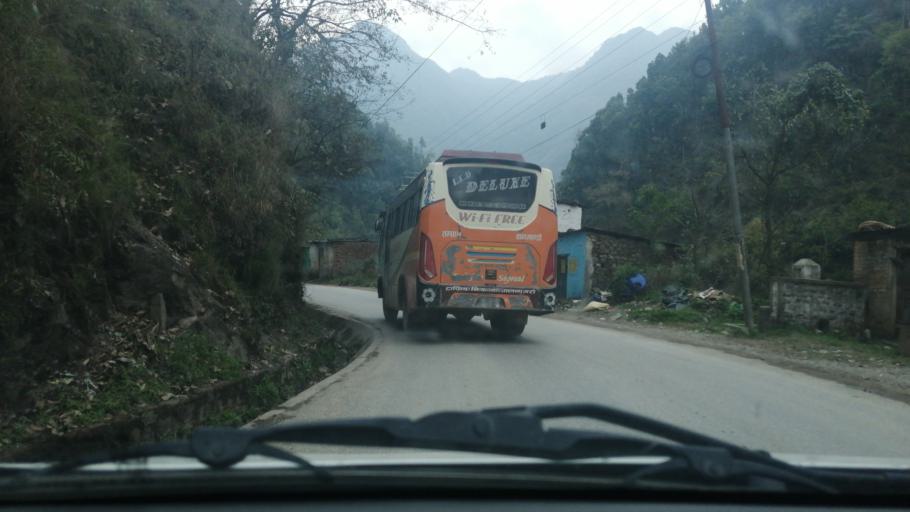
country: NP
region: Western Region
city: Tansen
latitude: 27.8063
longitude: 83.5147
